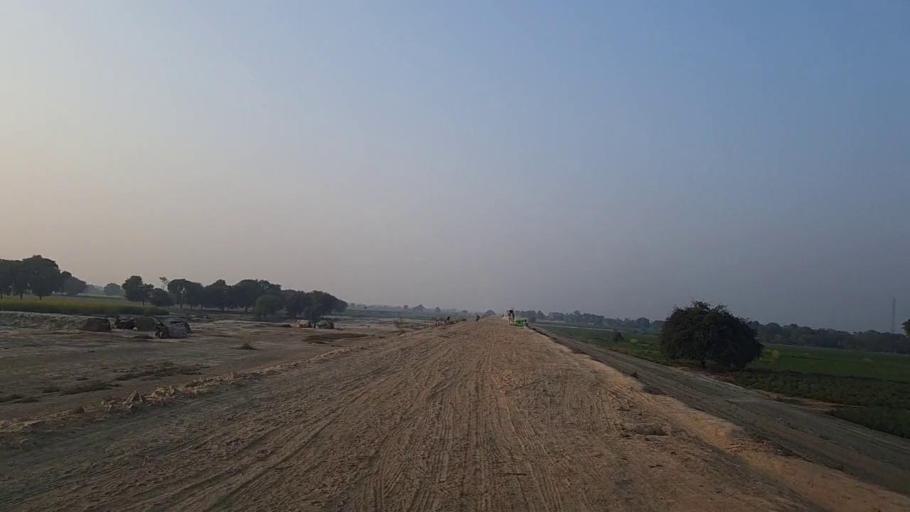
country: PK
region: Sindh
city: Sann
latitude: 26.1872
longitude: 68.0926
